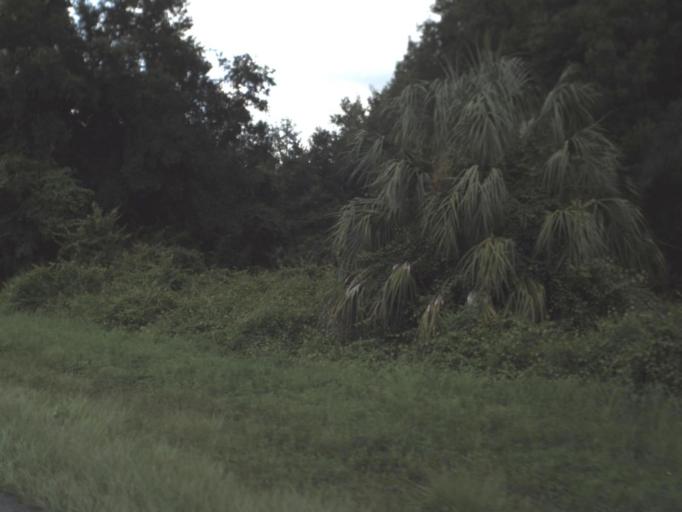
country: US
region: Florida
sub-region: Citrus County
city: Inverness Highlands North
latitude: 28.8802
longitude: -82.3643
